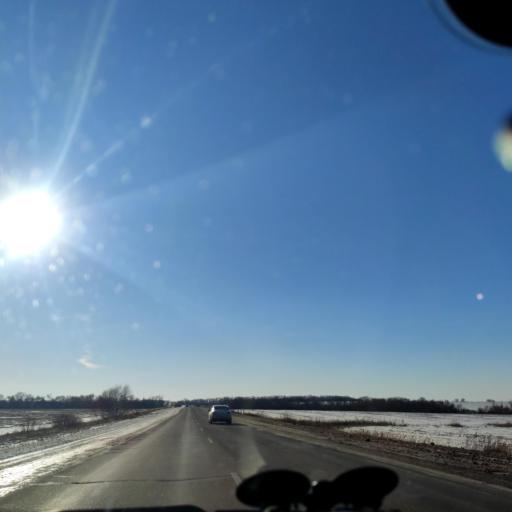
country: RU
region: Voronezj
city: Devitsa
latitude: 51.5843
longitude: 38.9758
